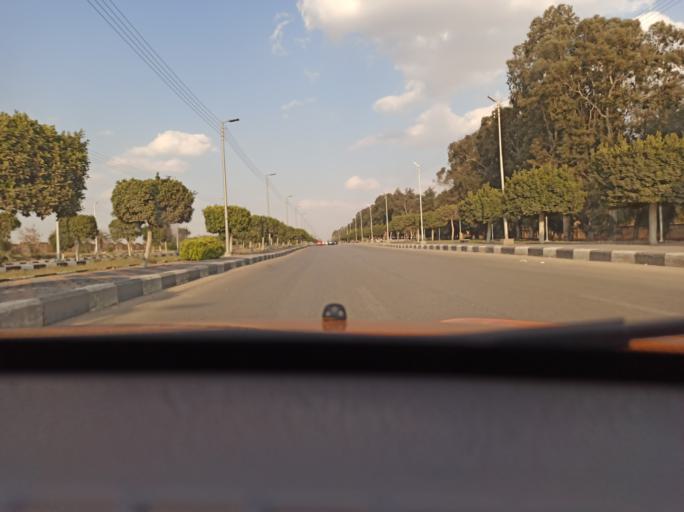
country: EG
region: Al Isma'iliyah
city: Ismailia
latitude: 30.6162
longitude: 32.2590
